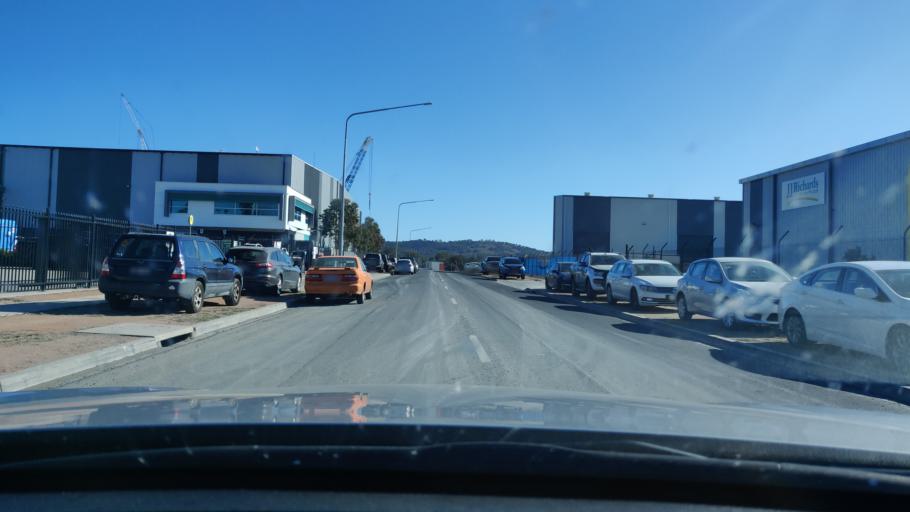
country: AU
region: Australian Capital Territory
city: Macarthur
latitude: -35.3993
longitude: 149.1620
